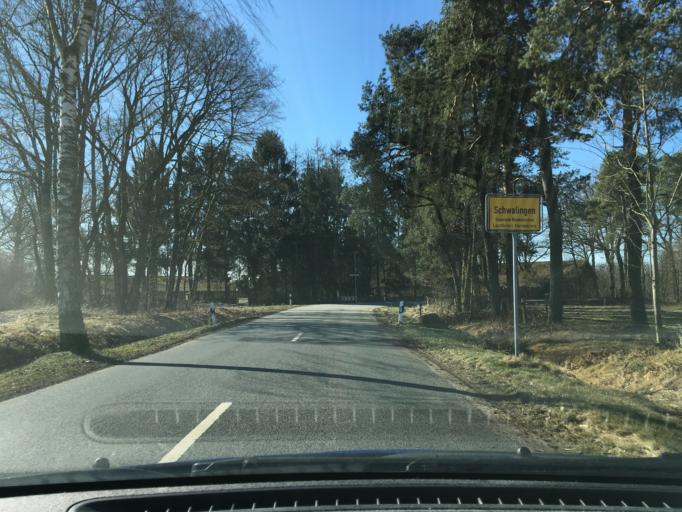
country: DE
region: Lower Saxony
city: Neuenkirchen
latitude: 53.0721
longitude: 9.7110
